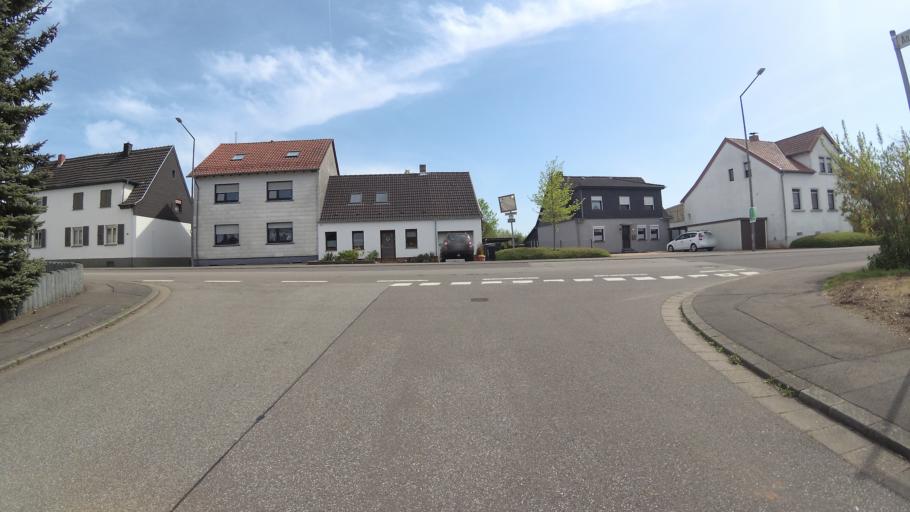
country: DE
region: Saarland
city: Homburg
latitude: 49.3506
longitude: 7.3227
